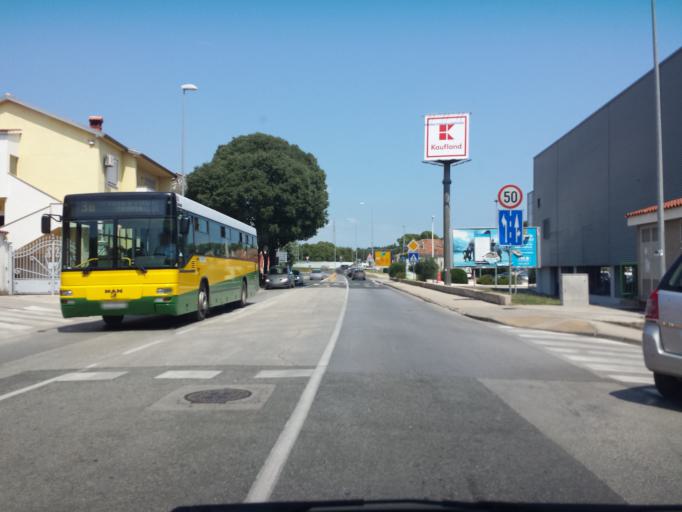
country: HR
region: Istarska
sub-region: Grad Pula
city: Pula
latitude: 44.8789
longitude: 13.8622
